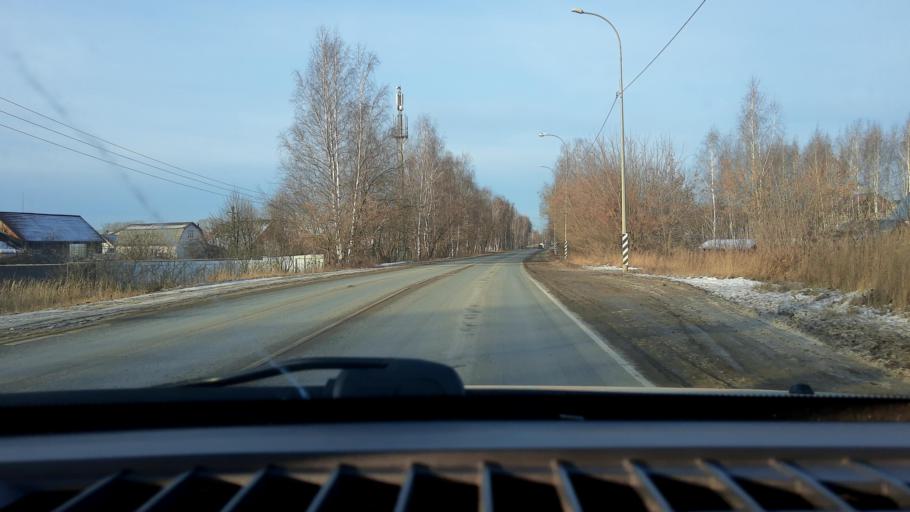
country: RU
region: Nizjnij Novgorod
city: Bor
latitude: 56.3796
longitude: 44.0433
